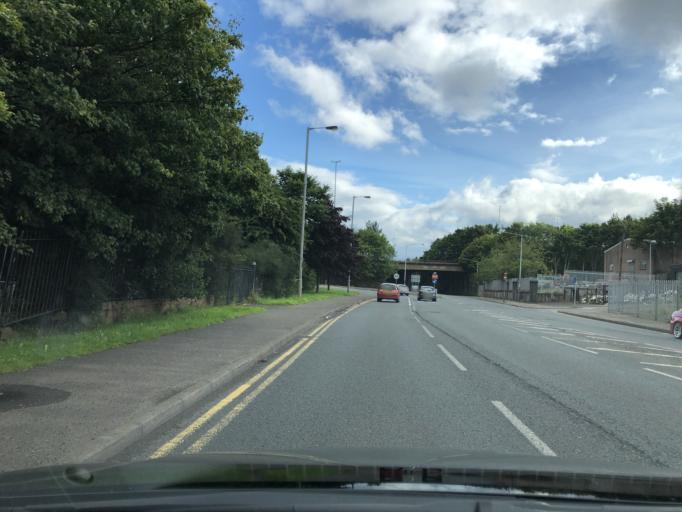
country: GB
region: Northern Ireland
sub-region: Newtownabbey District
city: Newtownabbey
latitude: 54.6500
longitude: -5.9187
